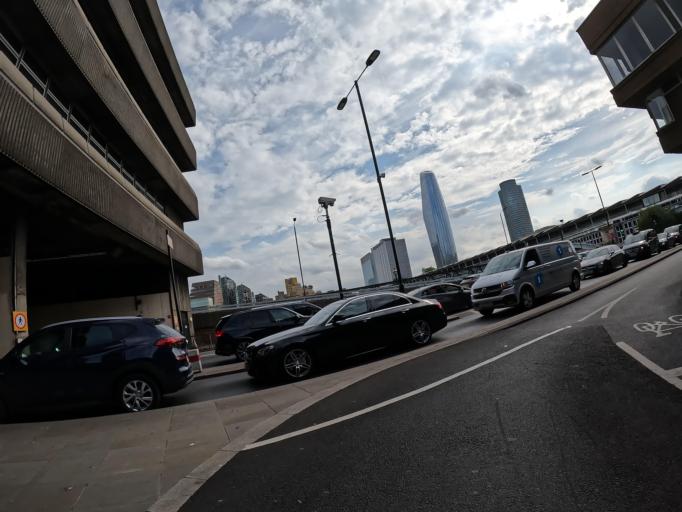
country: GB
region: England
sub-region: Greater London
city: Harringay
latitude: 51.5768
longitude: -0.0857
